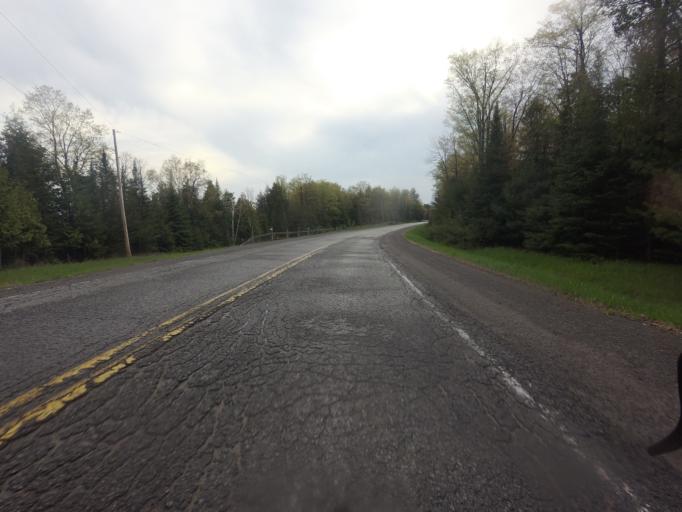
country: CA
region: Ontario
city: Carleton Place
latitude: 45.1853
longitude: -76.3501
